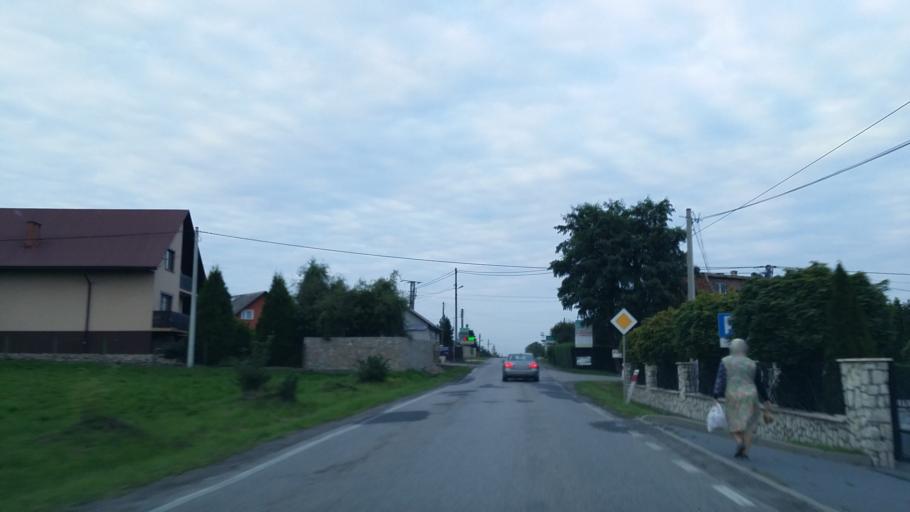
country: PL
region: Lesser Poland Voivodeship
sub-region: Powiat krakowski
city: Kaszow
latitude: 50.0146
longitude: 19.7173
